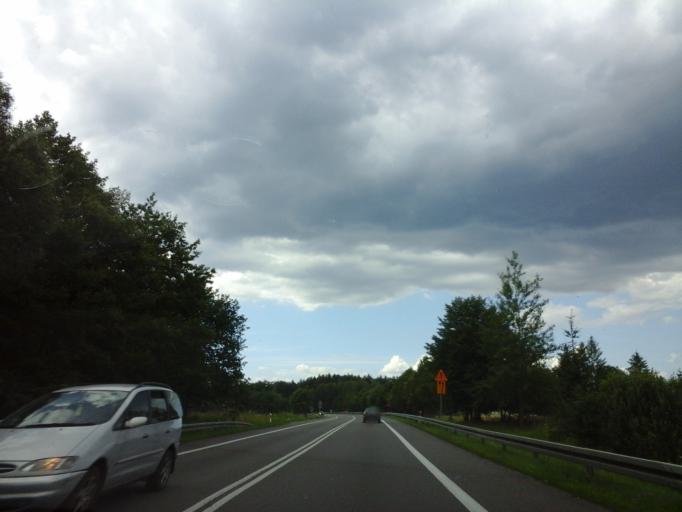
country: PL
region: West Pomeranian Voivodeship
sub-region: Powiat goleniowski
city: Przybiernow
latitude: 53.6800
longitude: 14.8102
